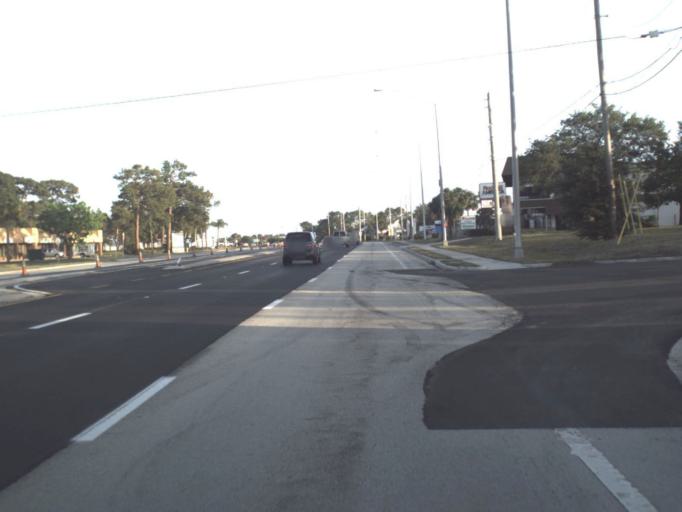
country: US
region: Florida
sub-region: Brevard County
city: Indian Harbour Beach
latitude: 28.1538
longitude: -80.6408
